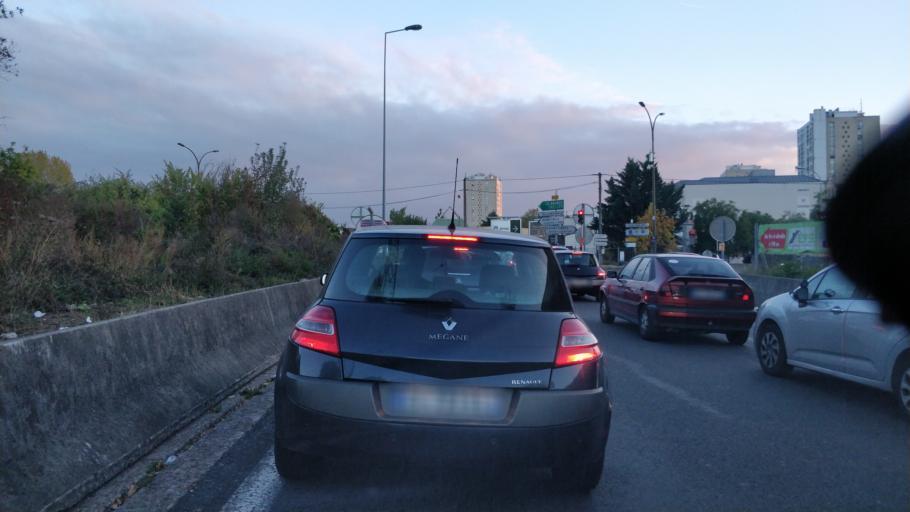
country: FR
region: Ile-de-France
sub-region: Departement de Seine-Saint-Denis
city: Villemomble
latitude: 48.8836
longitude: 2.4919
